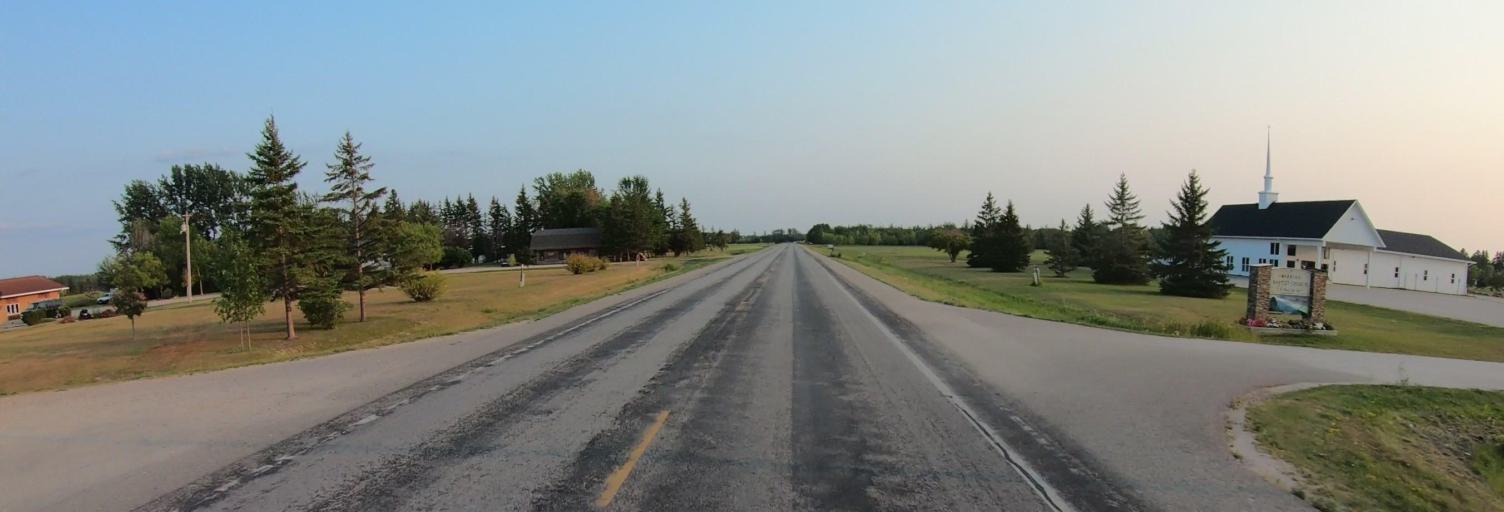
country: US
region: Minnesota
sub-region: Roseau County
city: Warroad
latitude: 48.8943
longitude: -95.3201
